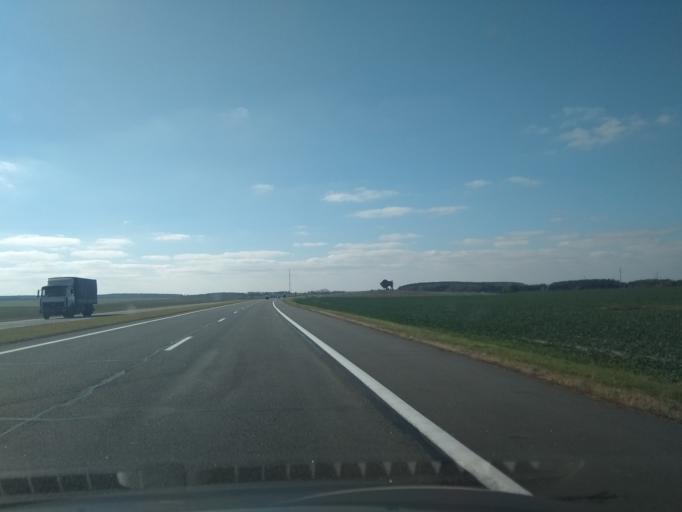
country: BY
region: Minsk
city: Snow
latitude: 53.3042
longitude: 26.3818
